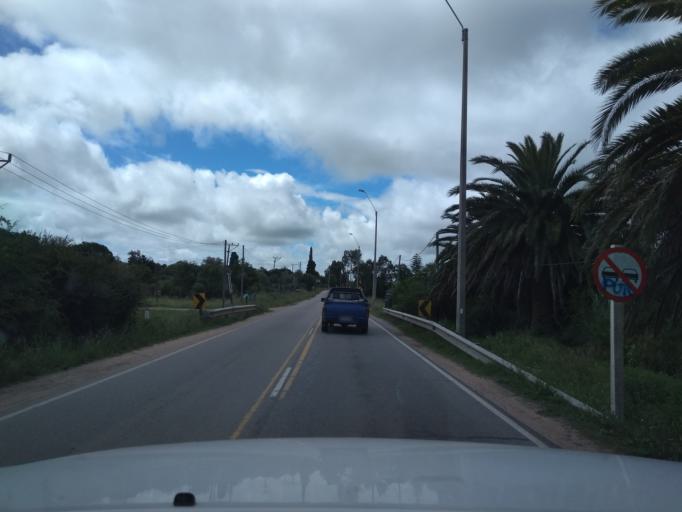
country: UY
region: Canelones
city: Pando
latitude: -34.6975
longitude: -55.9672
